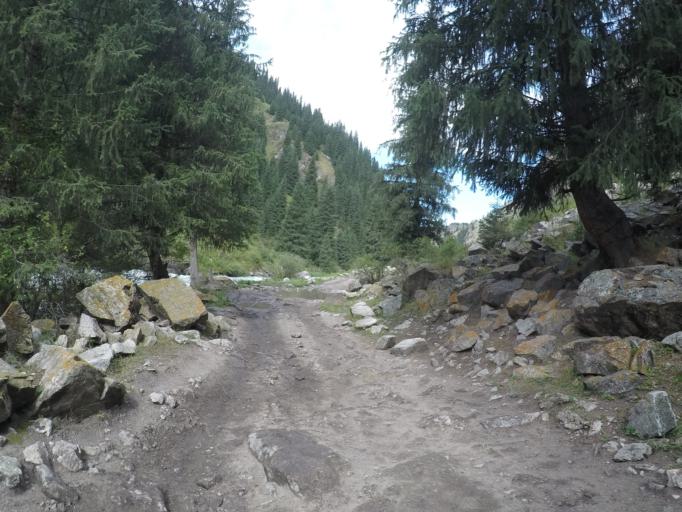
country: KG
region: Ysyk-Koel
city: Teploklyuchenka
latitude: 42.4383
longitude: 78.5596
